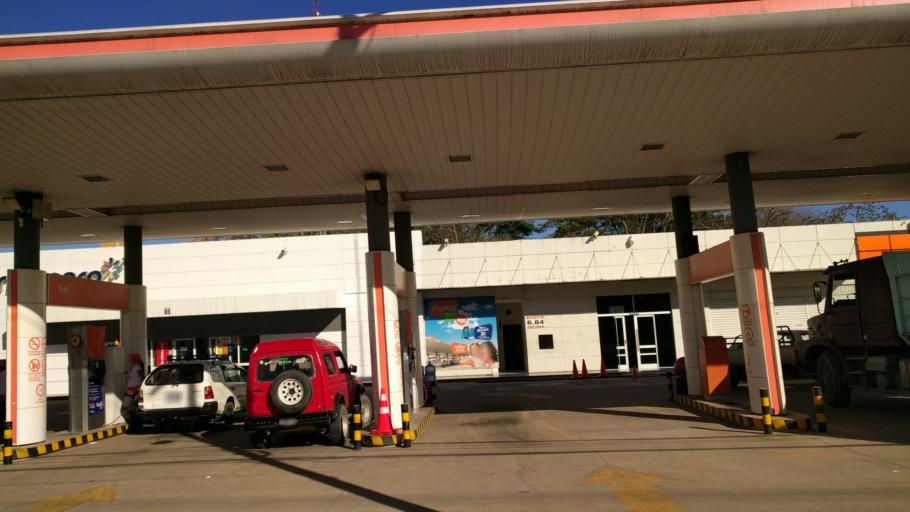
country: BO
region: Santa Cruz
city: Santa Cruz de la Sierra
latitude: -17.7543
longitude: -63.1969
